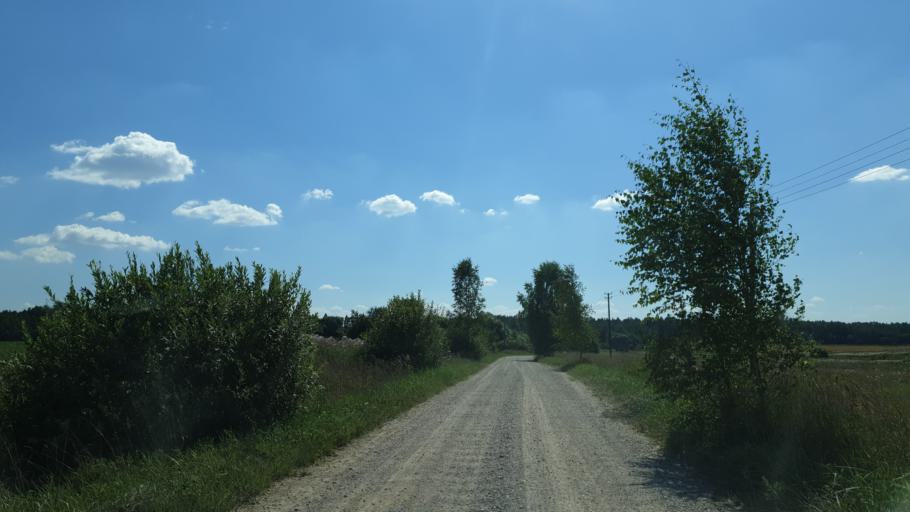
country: LT
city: Sirvintos
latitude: 54.9054
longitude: 24.9110
